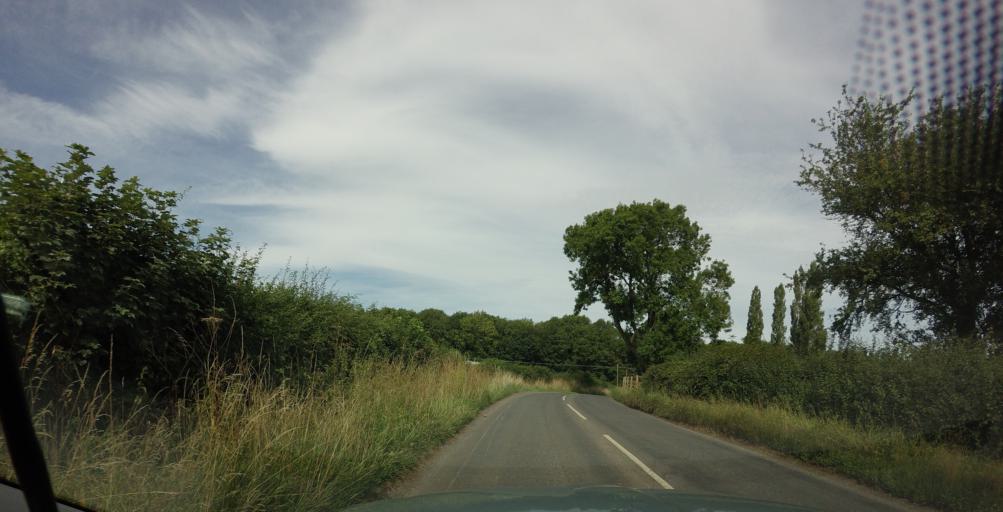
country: GB
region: England
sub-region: North Yorkshire
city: Ripon
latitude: 54.0984
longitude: -1.5119
